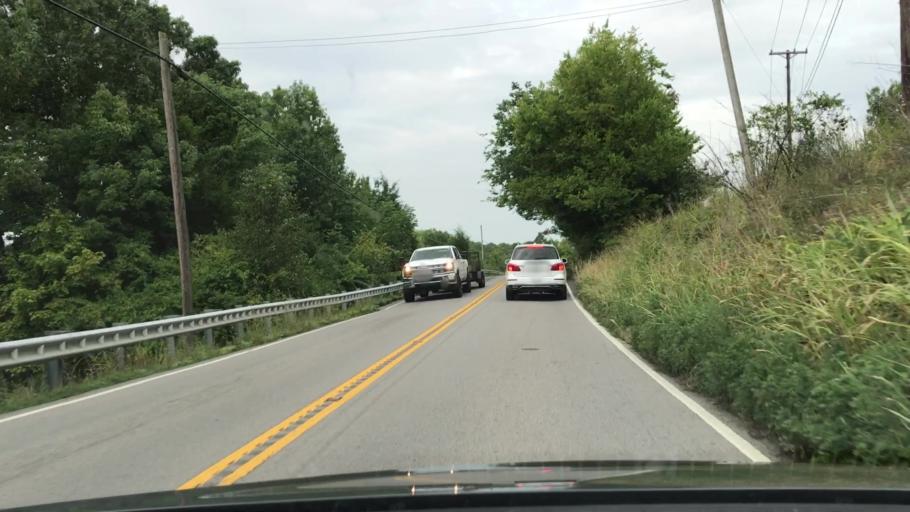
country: US
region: Tennessee
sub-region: Williamson County
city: Franklin
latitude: 35.9336
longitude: -86.7798
